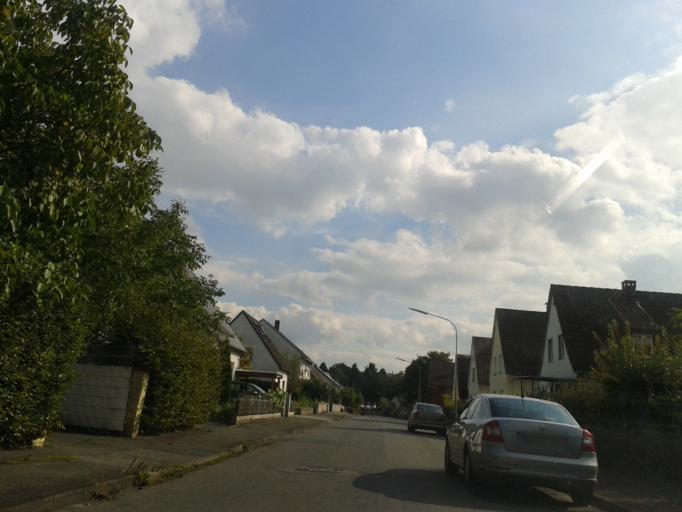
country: DE
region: North Rhine-Westphalia
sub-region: Regierungsbezirk Detmold
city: Schlangen
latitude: 51.8023
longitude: 8.8315
